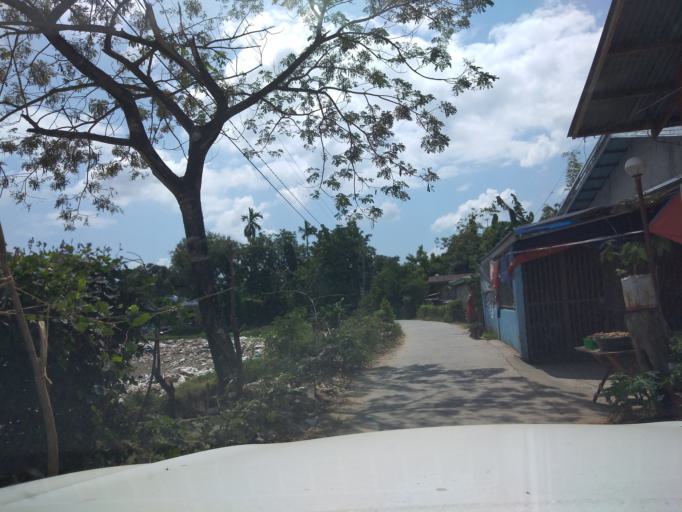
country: PH
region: Central Luzon
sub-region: Province of Pampanga
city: Lourdes
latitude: 15.0171
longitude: 120.8564
